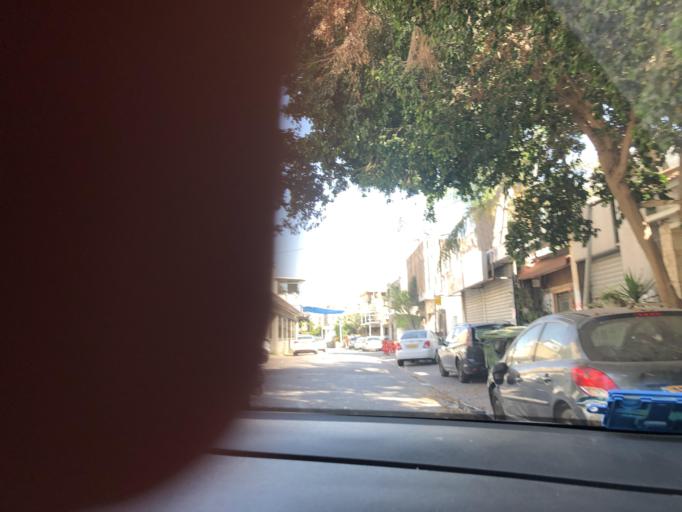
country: IL
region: Central District
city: Jaljulya
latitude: 32.1546
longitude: 34.9518
